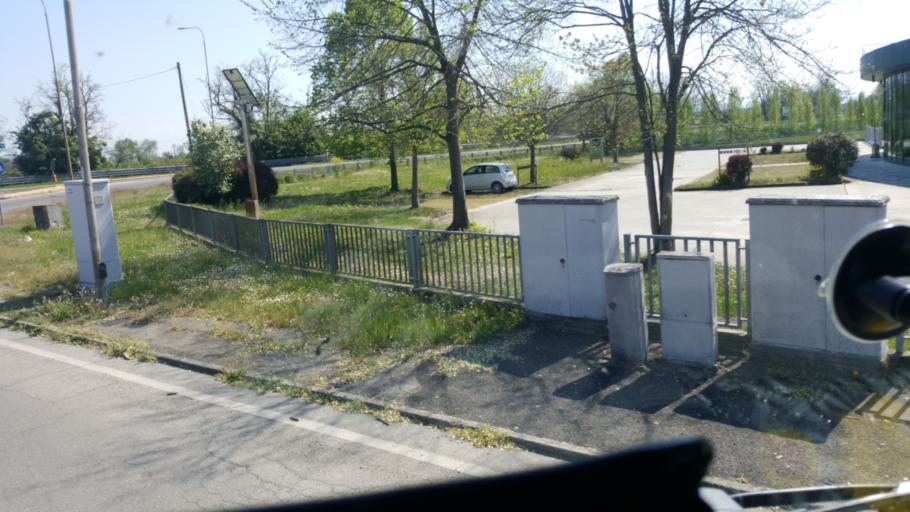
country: IT
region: Emilia-Romagna
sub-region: Provincia di Reggio Emilia
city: Bagnolo in Piano
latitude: 44.7334
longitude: 10.6541
